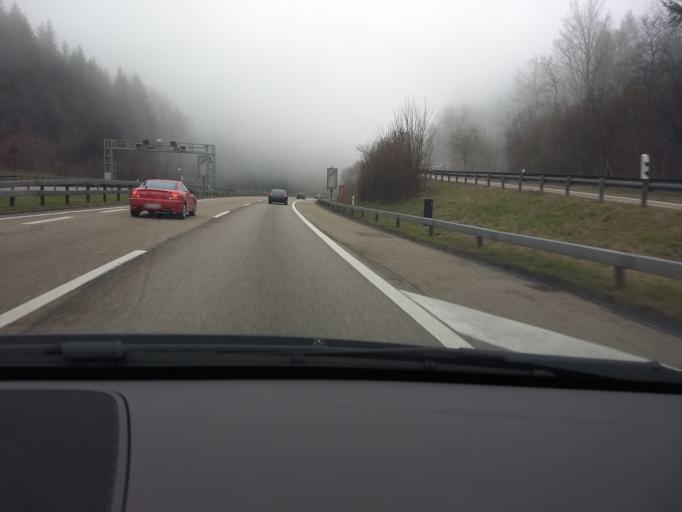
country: CH
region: Basel-Landschaft
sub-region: Bezirk Liestal
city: Lausen
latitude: 47.4895
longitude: 7.7738
